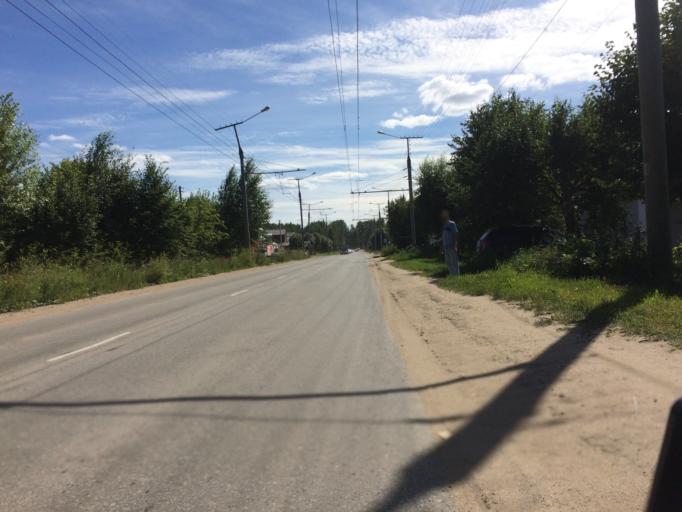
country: RU
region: Mariy-El
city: Yoshkar-Ola
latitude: 56.6450
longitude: 47.9542
